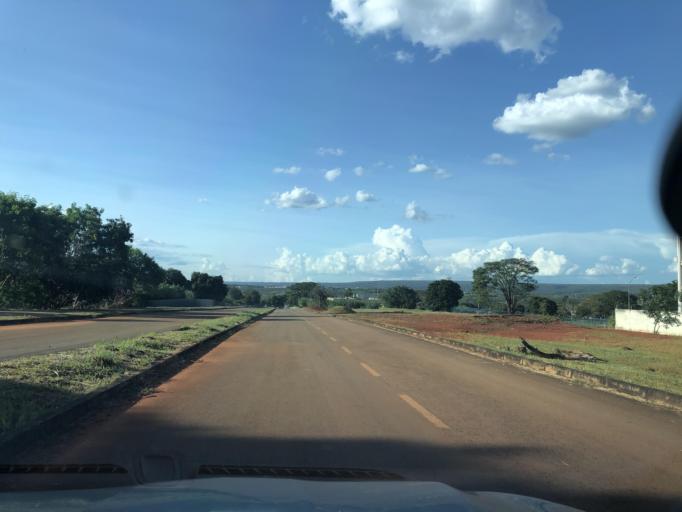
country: BR
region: Federal District
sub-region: Brasilia
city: Brasilia
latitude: -15.7427
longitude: -47.9040
